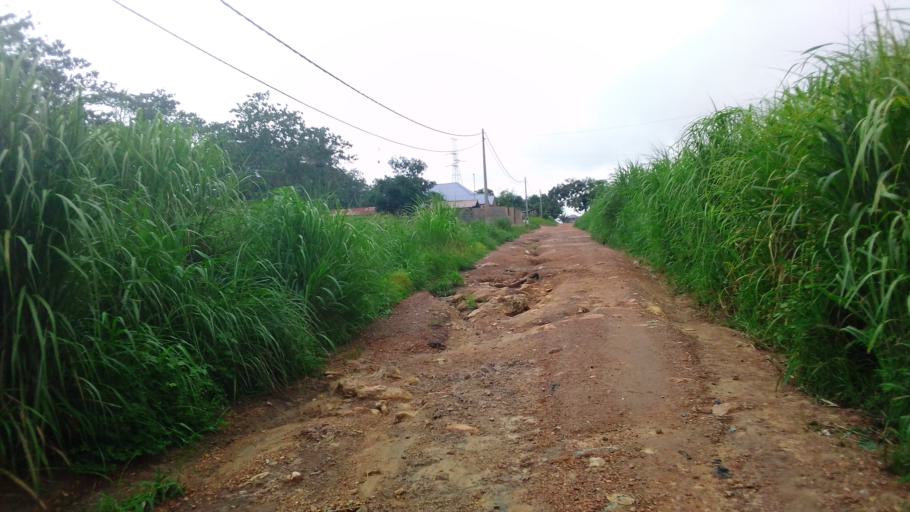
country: SL
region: Northern Province
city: Lunsar
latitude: 8.6910
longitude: -12.5475
